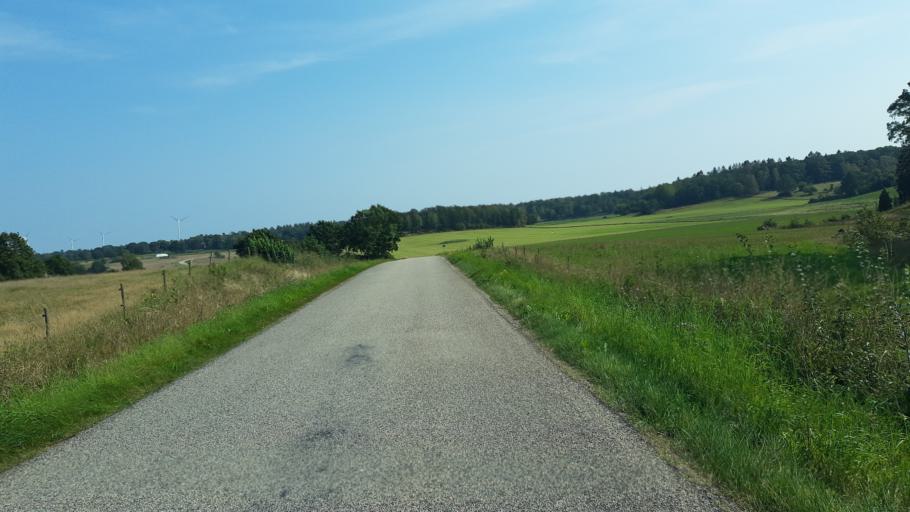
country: SE
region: Blekinge
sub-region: Ronneby Kommun
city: Brakne-Hoby
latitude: 56.1973
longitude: 15.1038
